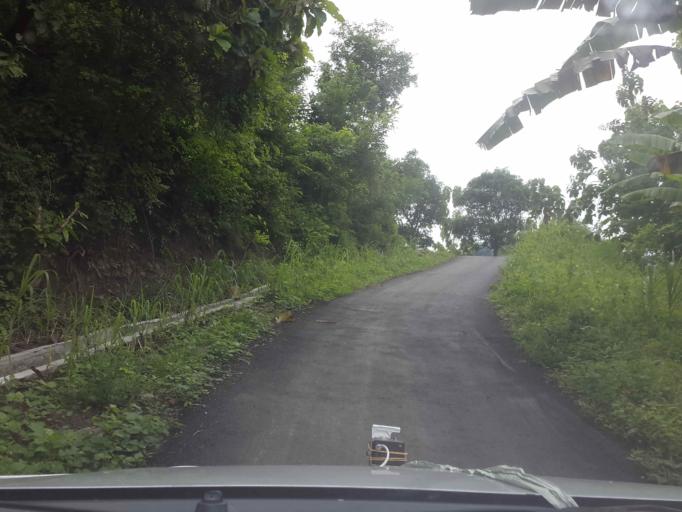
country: ID
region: East Java
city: Nganjuk
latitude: -7.4740
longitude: 111.7674
